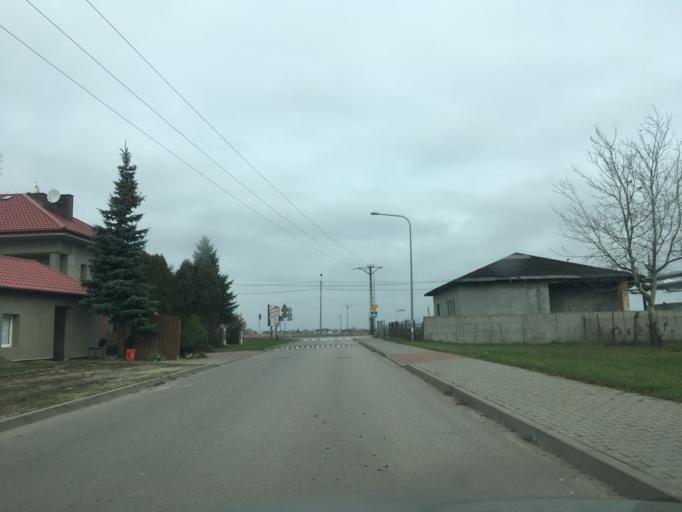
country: PL
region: Masovian Voivodeship
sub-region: Powiat piaseczynski
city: Lesznowola
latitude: 52.0822
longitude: 20.9611
